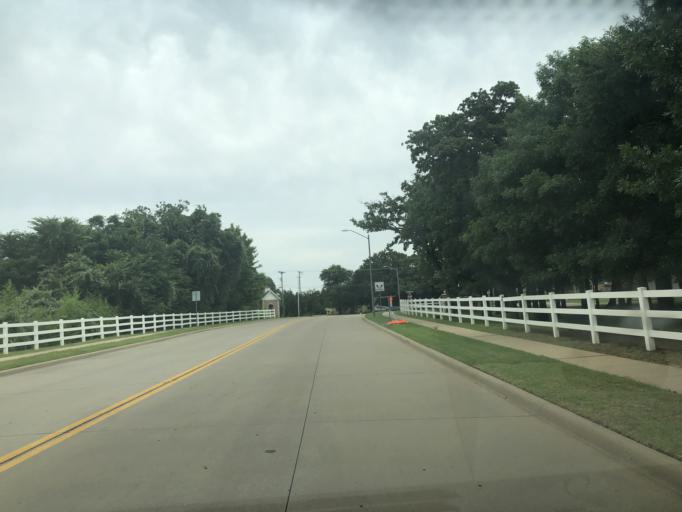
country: US
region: Texas
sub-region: Dallas County
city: Irving
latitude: 32.8031
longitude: -96.9920
